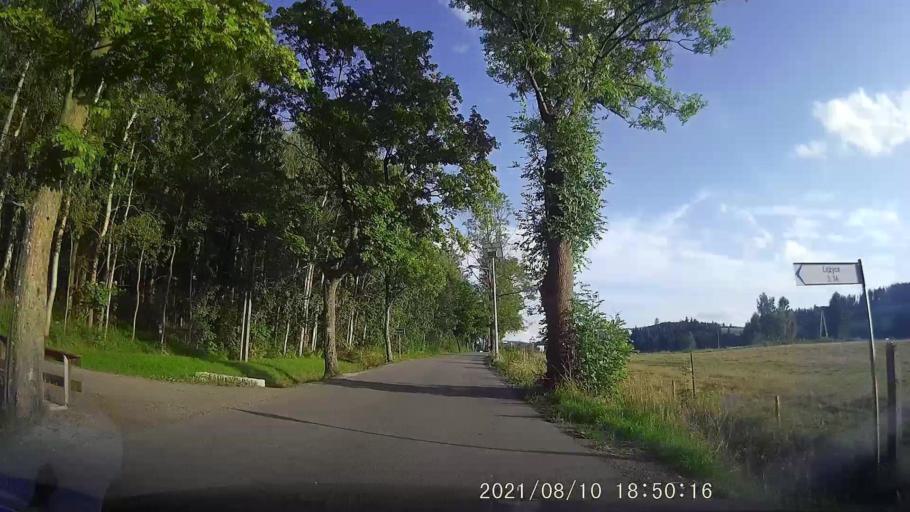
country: PL
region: Lower Silesian Voivodeship
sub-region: Powiat klodzki
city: Duszniki-Zdroj
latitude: 50.4205
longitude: 16.3762
